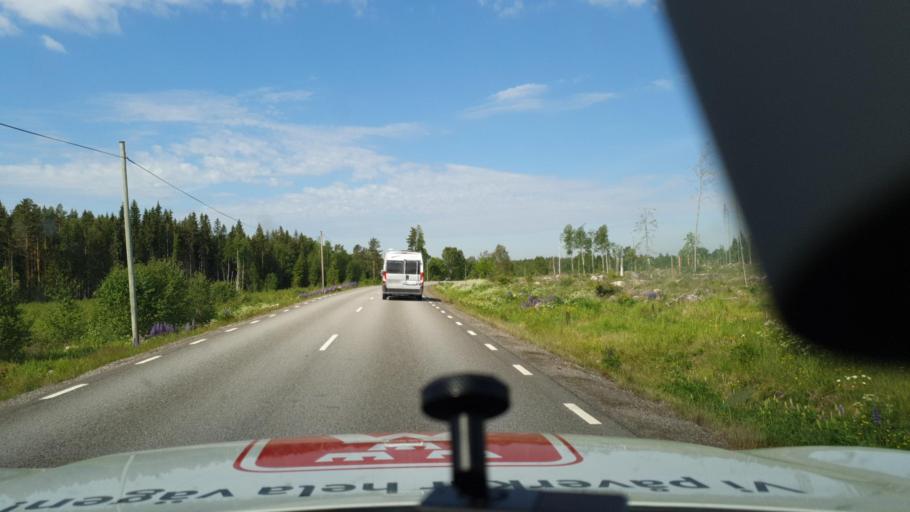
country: SE
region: Vaermland
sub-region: Arvika Kommun
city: Arvika
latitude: 59.8719
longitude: 12.5972
